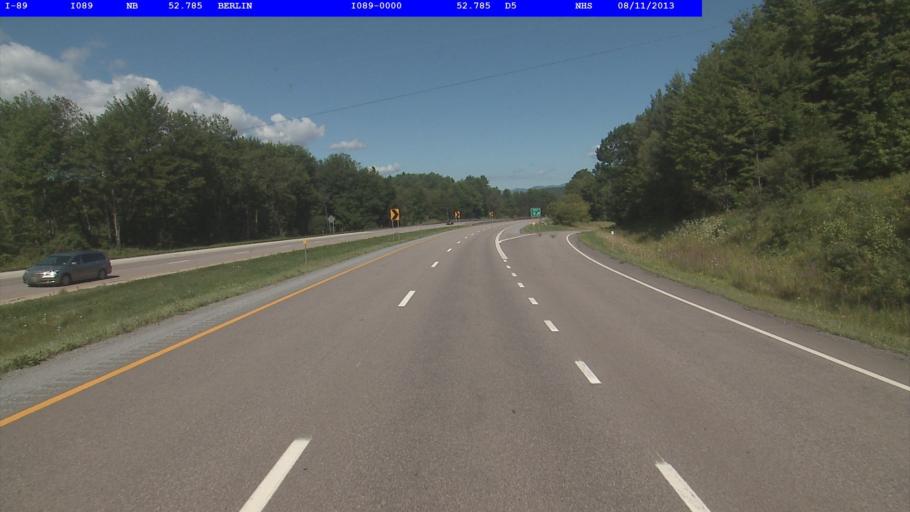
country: US
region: Vermont
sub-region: Washington County
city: Montpelier
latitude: 44.2490
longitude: -72.5934
